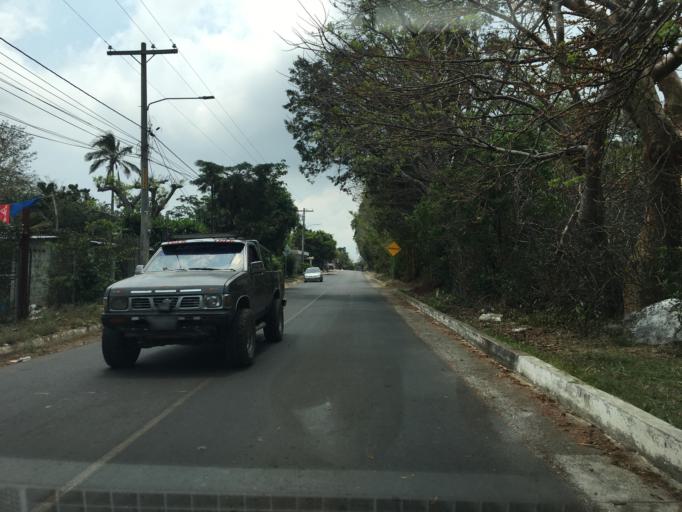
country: GT
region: Escuintla
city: San Vicente Pacaya
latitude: 14.3464
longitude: -90.5711
